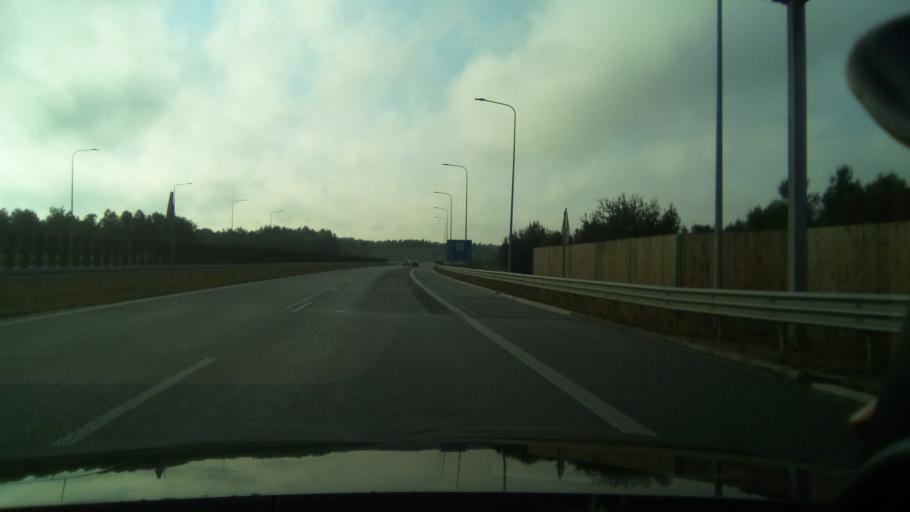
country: PL
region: Silesian Voivodeship
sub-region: Powiat czestochowski
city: Konopiska
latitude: 50.7414
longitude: 19.0503
